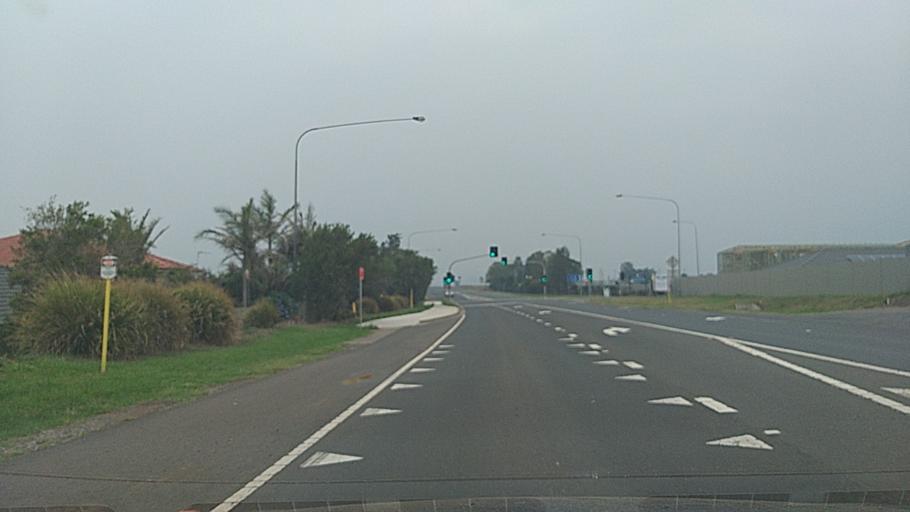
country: AU
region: New South Wales
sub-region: Shellharbour
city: Croom
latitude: -34.5931
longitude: 150.8484
